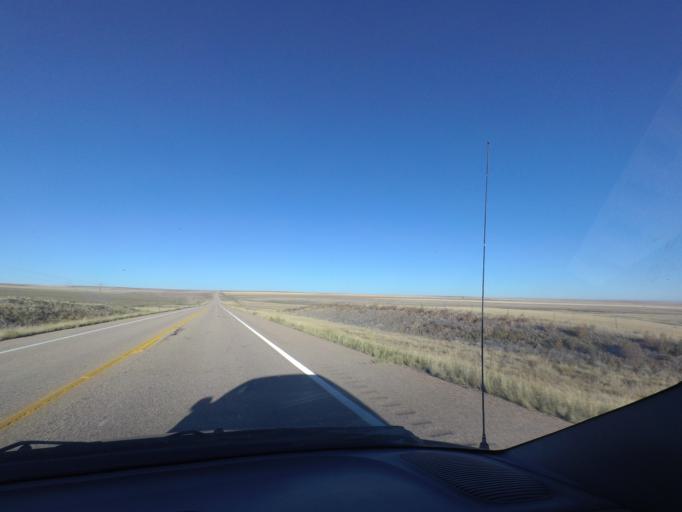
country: US
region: Colorado
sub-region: Lincoln County
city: Limon
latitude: 39.7399
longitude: -103.7486
